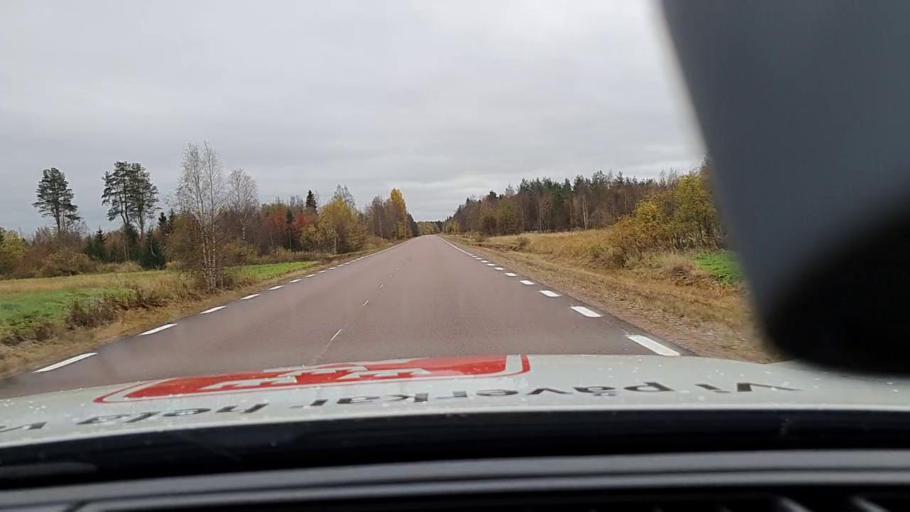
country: FI
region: Lapland
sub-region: Kemi-Tornio
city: Tornio
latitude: 66.0563
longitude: 23.9332
